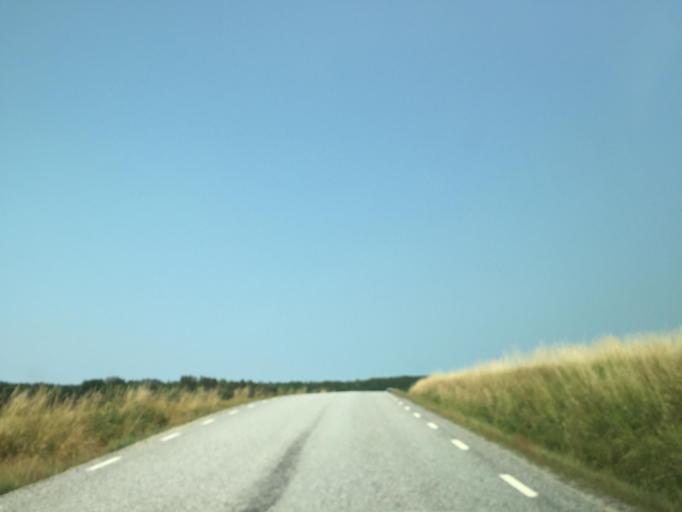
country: SE
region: Vaestra Goetaland
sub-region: Lilla Edets Kommun
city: Lilla Edet
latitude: 58.2051
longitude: 12.1259
